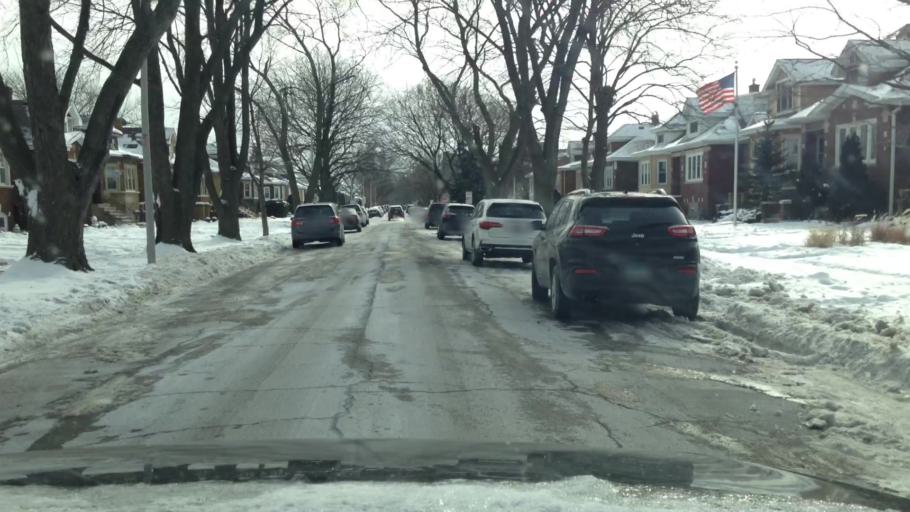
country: US
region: Illinois
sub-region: Cook County
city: Elmwood Park
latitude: 41.9372
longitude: -87.8177
